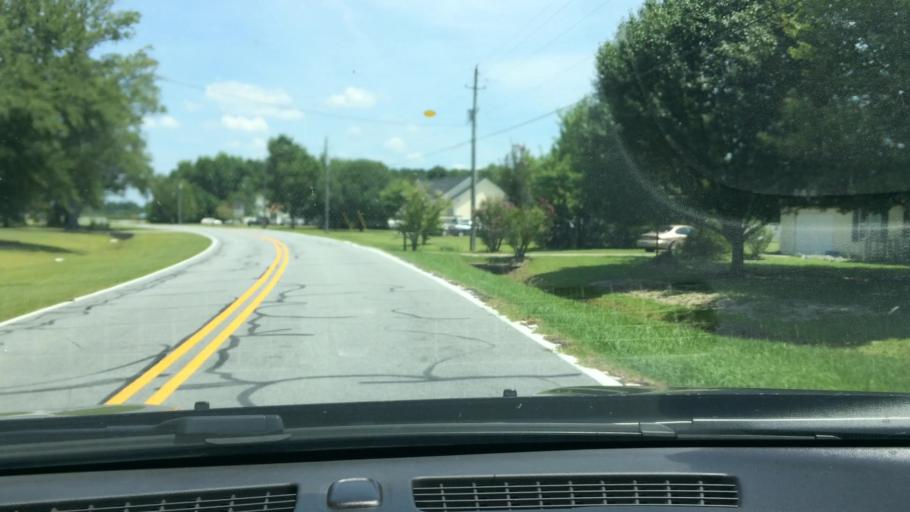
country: US
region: North Carolina
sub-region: Pitt County
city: Windsor
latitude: 35.5060
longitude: -77.3239
